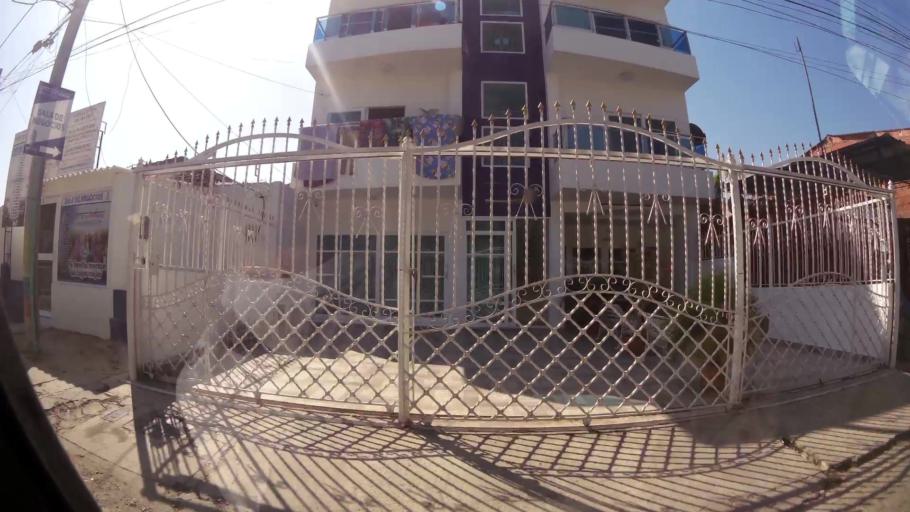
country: CO
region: Bolivar
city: Cartagena
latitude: 10.3846
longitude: -75.4648
